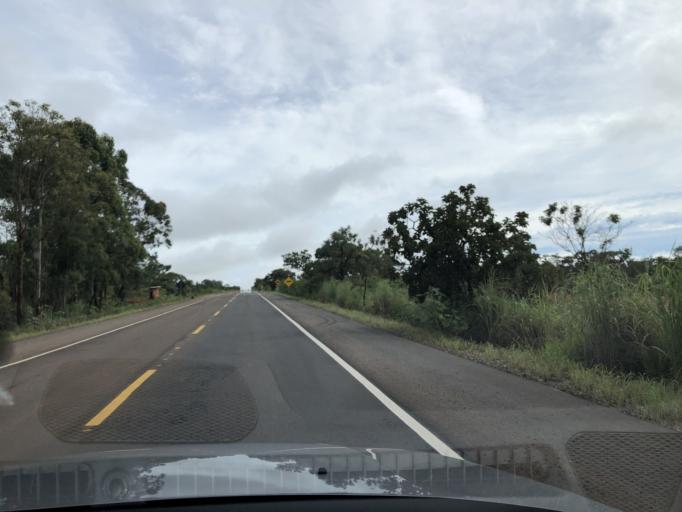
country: BR
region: Federal District
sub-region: Brasilia
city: Brasilia
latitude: -15.6466
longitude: -48.0808
